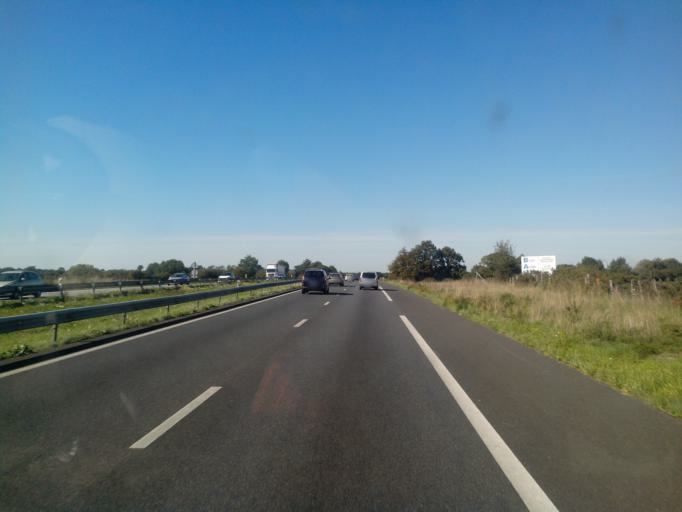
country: FR
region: Pays de la Loire
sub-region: Departement de la Loire-Atlantique
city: Vigneux-de-Bretagne
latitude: 47.3075
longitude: -1.7626
